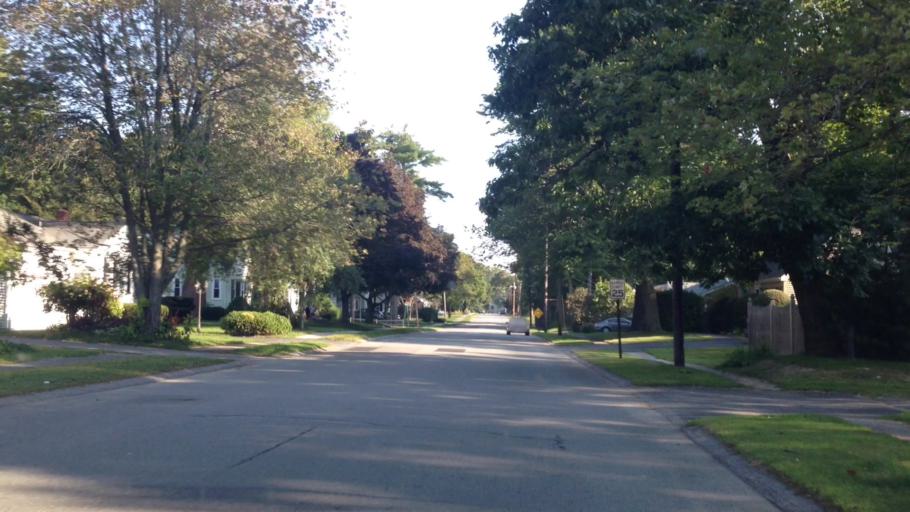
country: US
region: Maine
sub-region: Cumberland County
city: Westbrook
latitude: 43.6712
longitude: -70.3593
